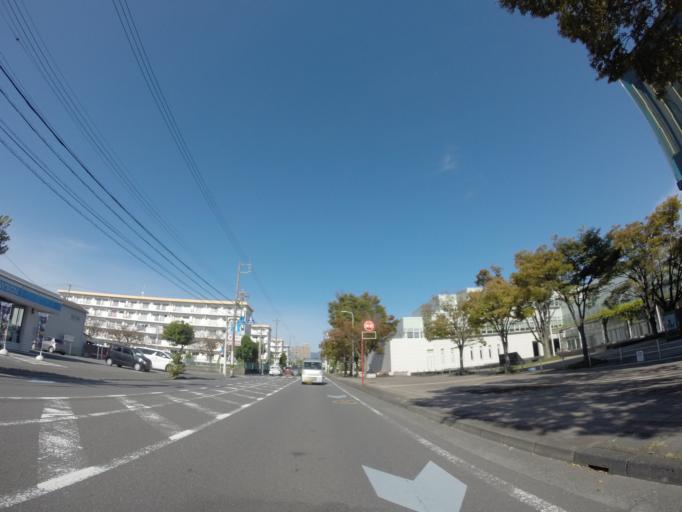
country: JP
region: Shizuoka
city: Shizuoka-shi
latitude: 34.9745
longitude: 138.4159
